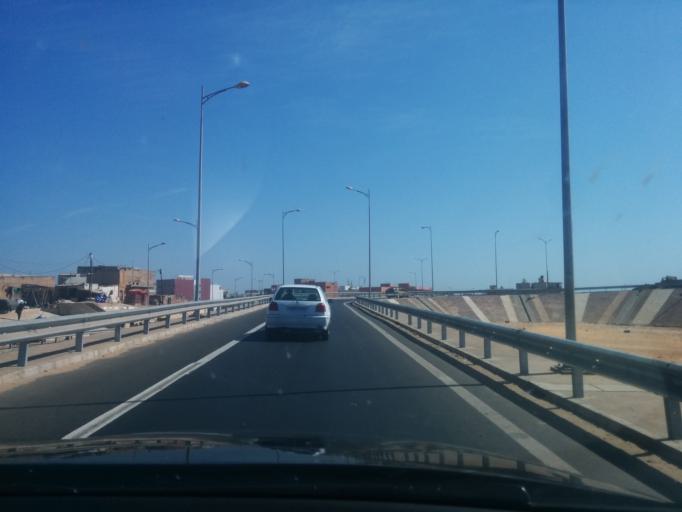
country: SN
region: Dakar
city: Grand Dakar
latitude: 14.7447
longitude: -17.4485
